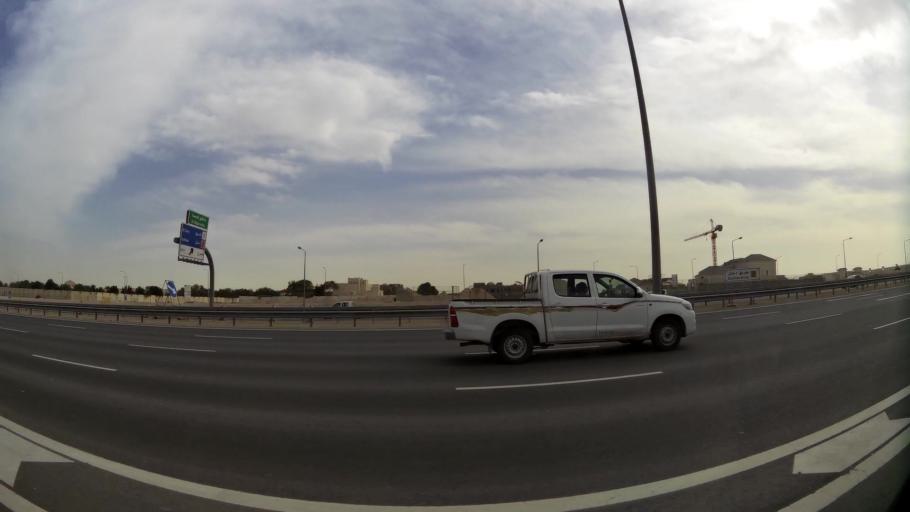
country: QA
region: Baladiyat ar Rayyan
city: Ar Rayyan
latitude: 25.3153
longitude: 51.3703
